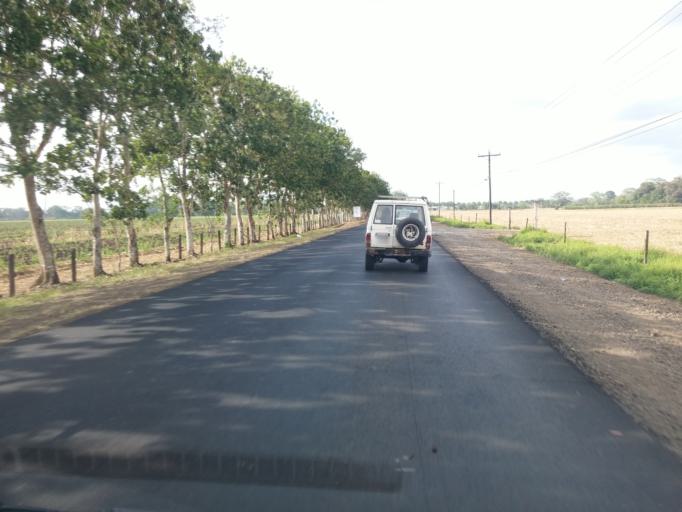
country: CR
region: Alajuela
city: Quesada
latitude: 10.4501
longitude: -84.4647
